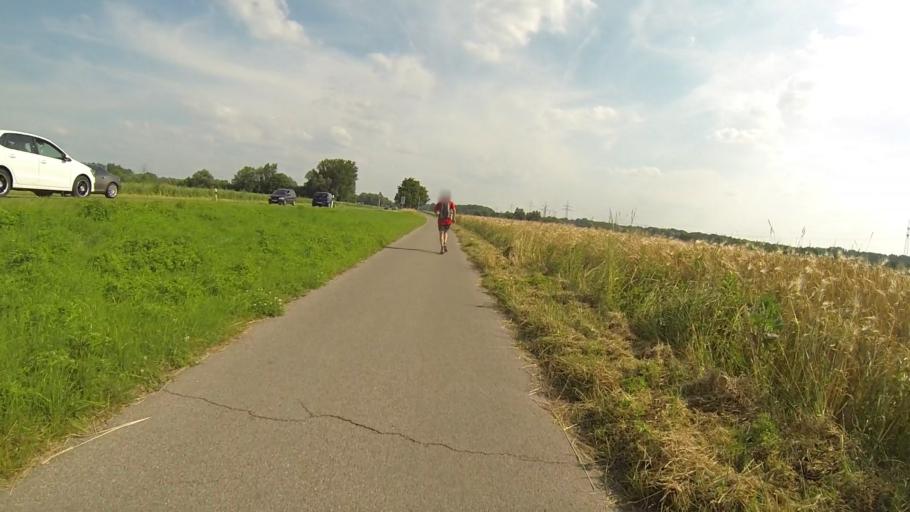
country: DE
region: Bavaria
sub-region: Swabia
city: Neu-Ulm
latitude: 48.3623
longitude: 10.0116
